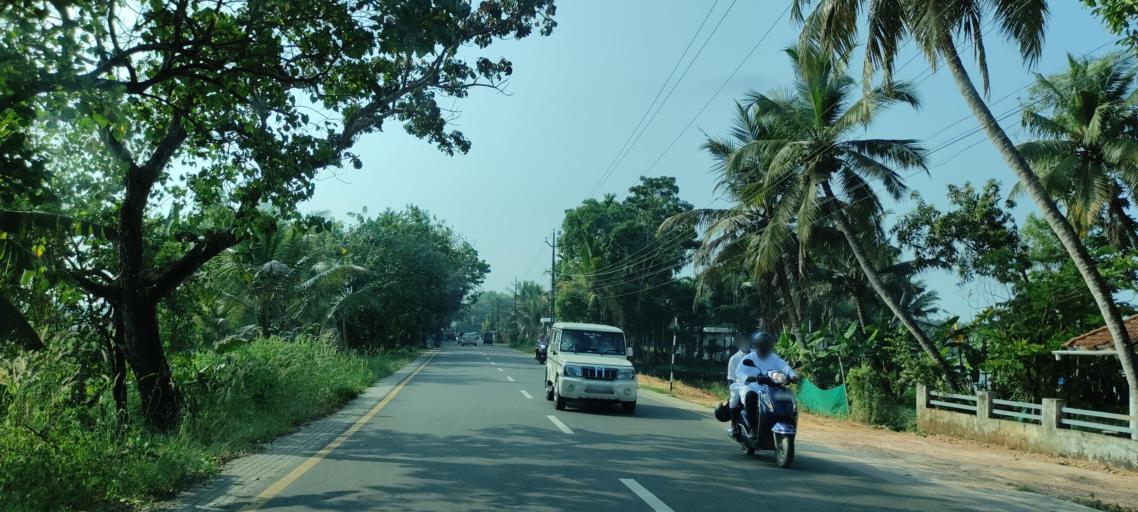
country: IN
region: Kerala
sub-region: Kottayam
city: Changanacheri
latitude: 9.3685
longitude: 76.4296
